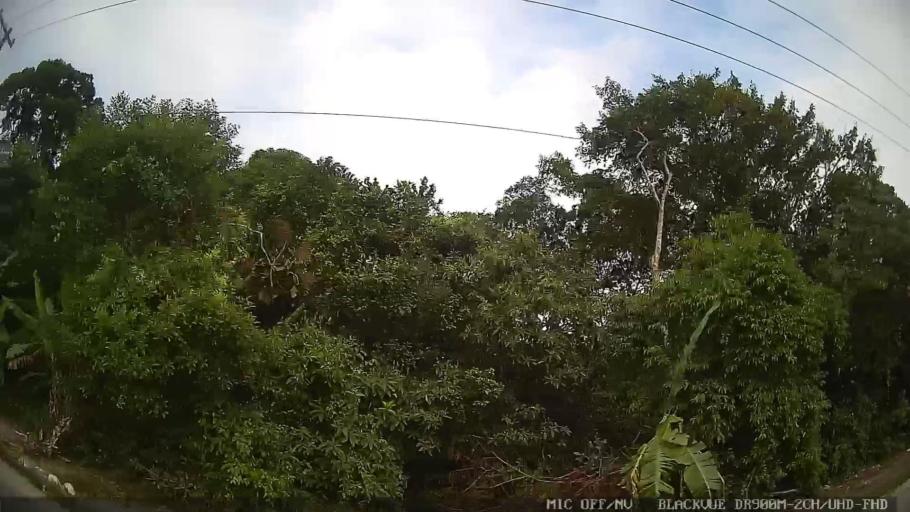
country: BR
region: Sao Paulo
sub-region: Guaruja
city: Guaruja
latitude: -23.9711
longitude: -46.2161
